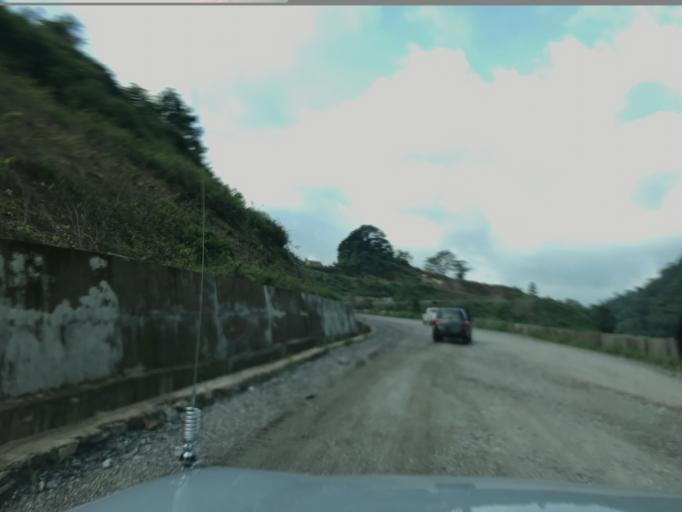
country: TL
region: Dili
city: Dili
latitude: -8.6364
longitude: 125.5096
